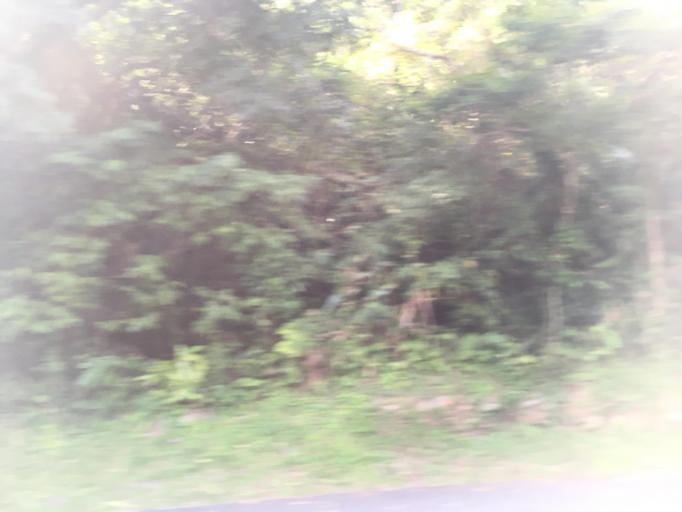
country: TW
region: Taiwan
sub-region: Yilan
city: Yilan
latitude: 24.6229
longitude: 121.5371
